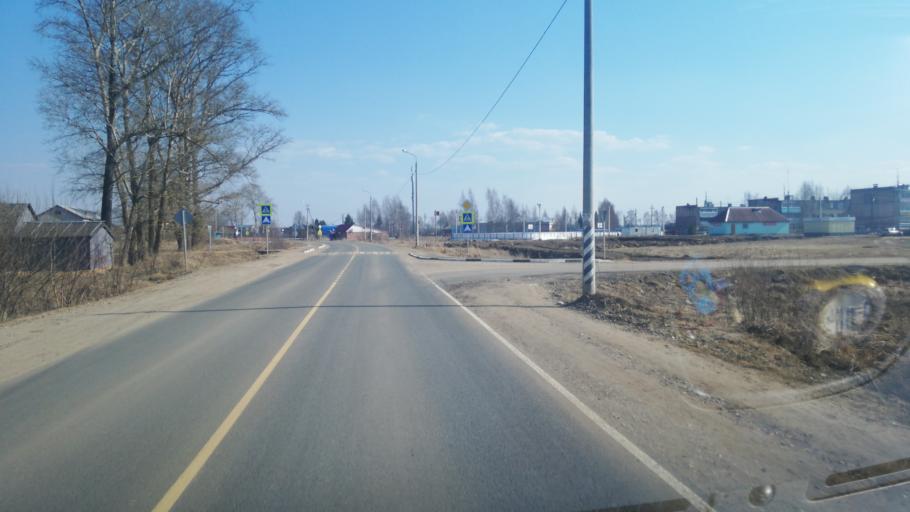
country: RU
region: Jaroslavl
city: Semibratovo
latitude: 57.2331
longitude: 39.4935
